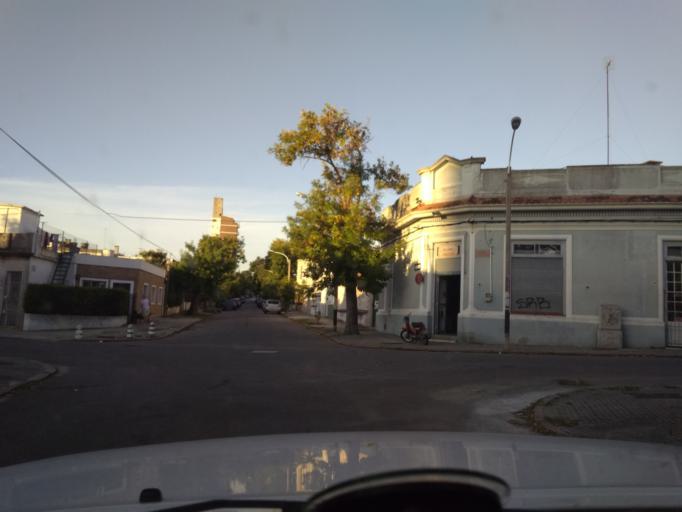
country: UY
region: Montevideo
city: Montevideo
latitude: -34.8903
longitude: -56.1452
